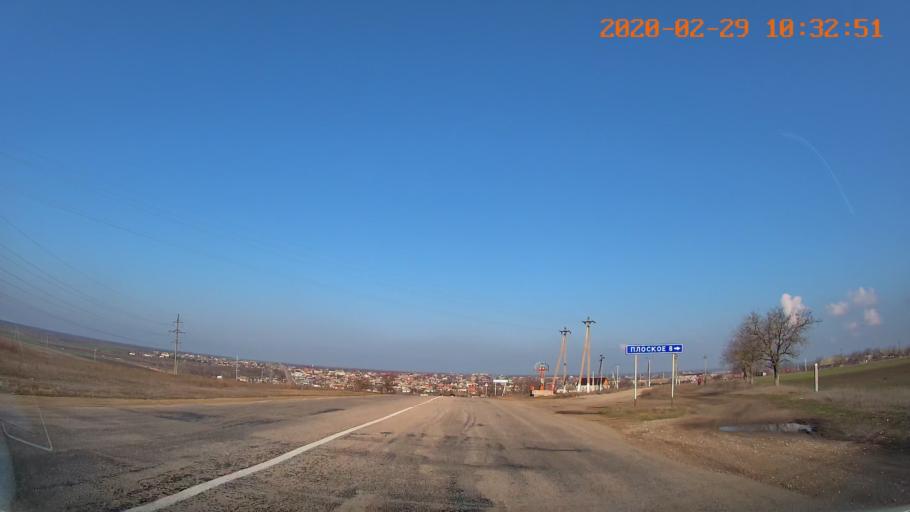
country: UA
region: Odessa
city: Velykoploske
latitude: 46.9659
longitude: 29.5506
